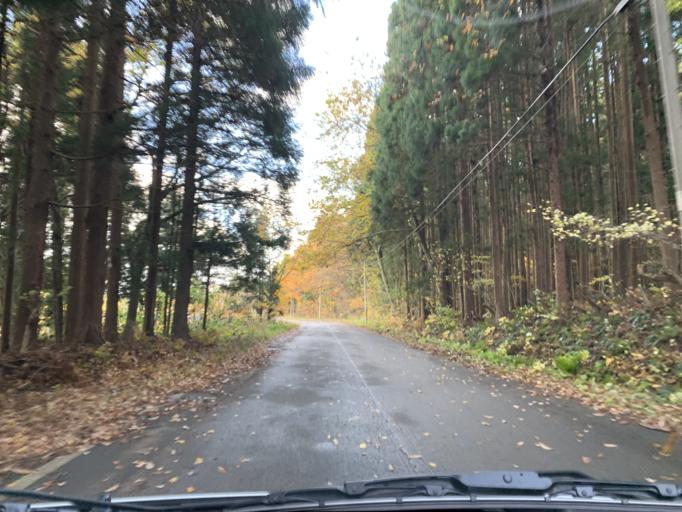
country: JP
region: Iwate
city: Mizusawa
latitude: 39.1051
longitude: 140.9764
